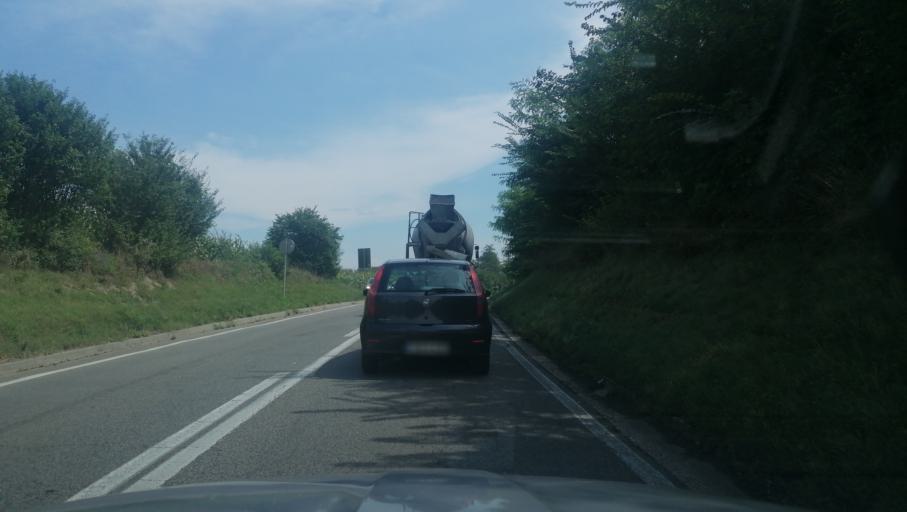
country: BA
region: Republika Srpska
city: Velika Obarska
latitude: 44.7692
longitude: 19.1281
